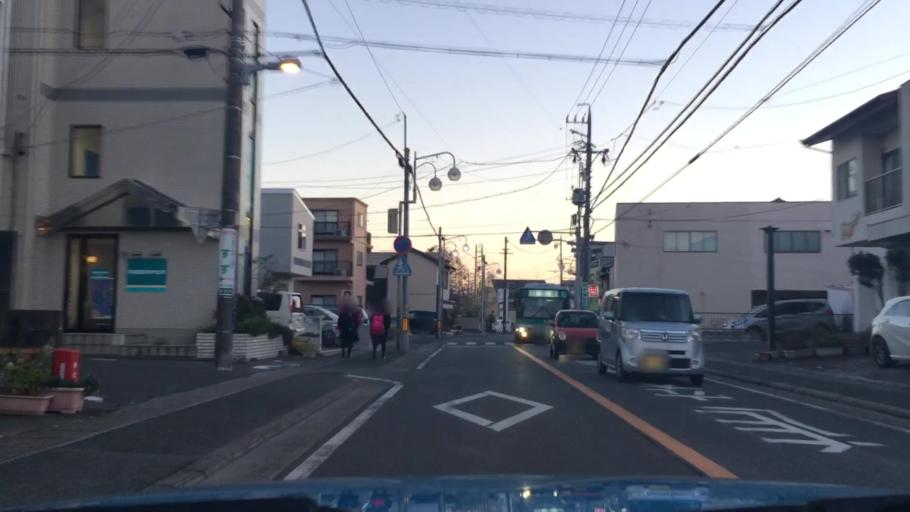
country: JP
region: Shizuoka
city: Hamamatsu
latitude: 34.7148
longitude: 137.7211
